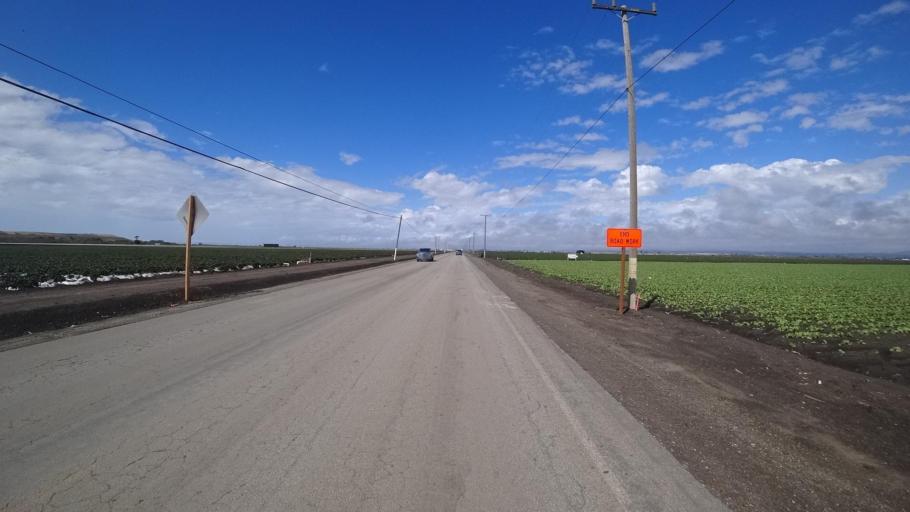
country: US
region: California
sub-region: Monterey County
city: Boronda
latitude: 36.6995
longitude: -121.7335
